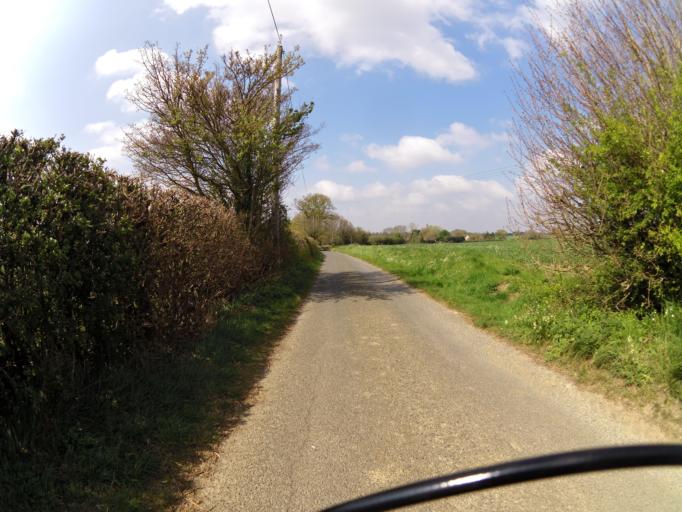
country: GB
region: England
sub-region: Suffolk
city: Bramford
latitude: 52.0795
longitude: 1.0332
